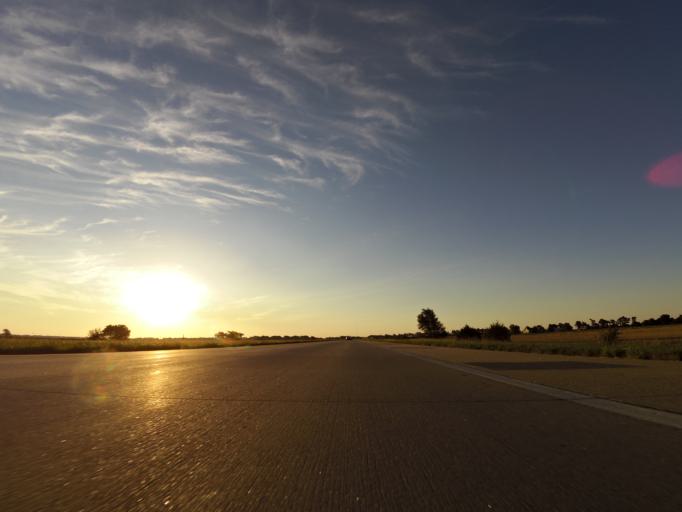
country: US
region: Kansas
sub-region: Reno County
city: Haven
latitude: 37.8801
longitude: -97.7138
